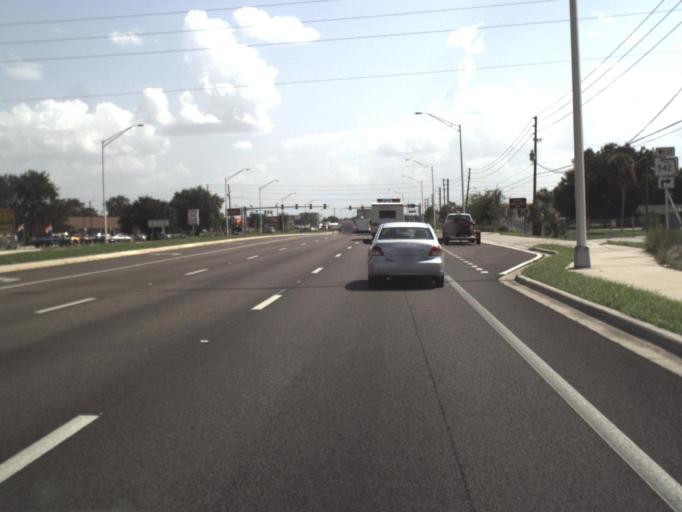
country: US
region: Florida
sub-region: Polk County
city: Dundee
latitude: 28.0211
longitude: -81.6332
